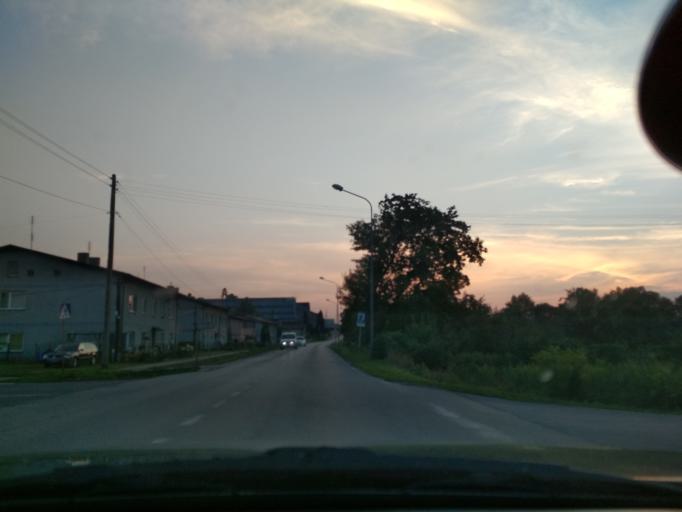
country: PL
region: Silesian Voivodeship
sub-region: Powiat zawiercianski
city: Pilica
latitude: 50.4684
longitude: 19.6827
